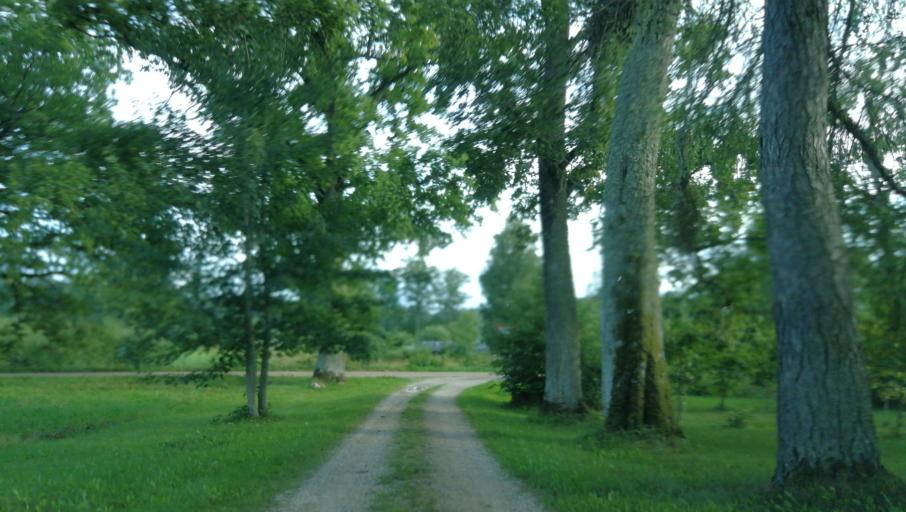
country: LV
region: Amatas Novads
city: Drabesi
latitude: 57.2552
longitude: 25.2836
